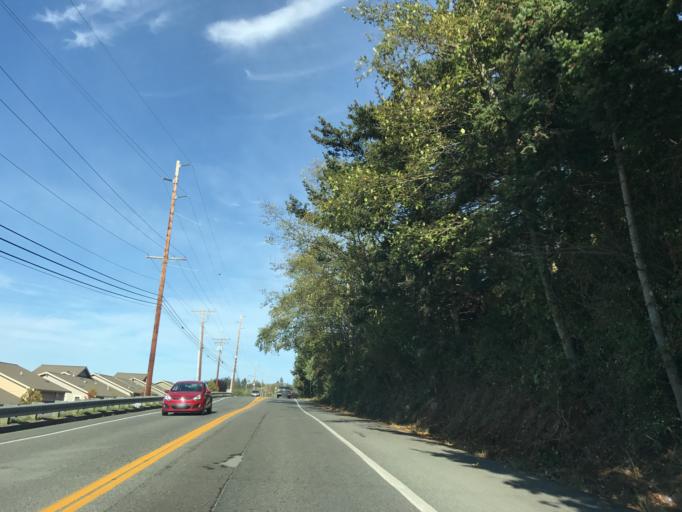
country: US
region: Washington
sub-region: Skagit County
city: Anacortes
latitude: 48.5000
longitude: -122.6722
